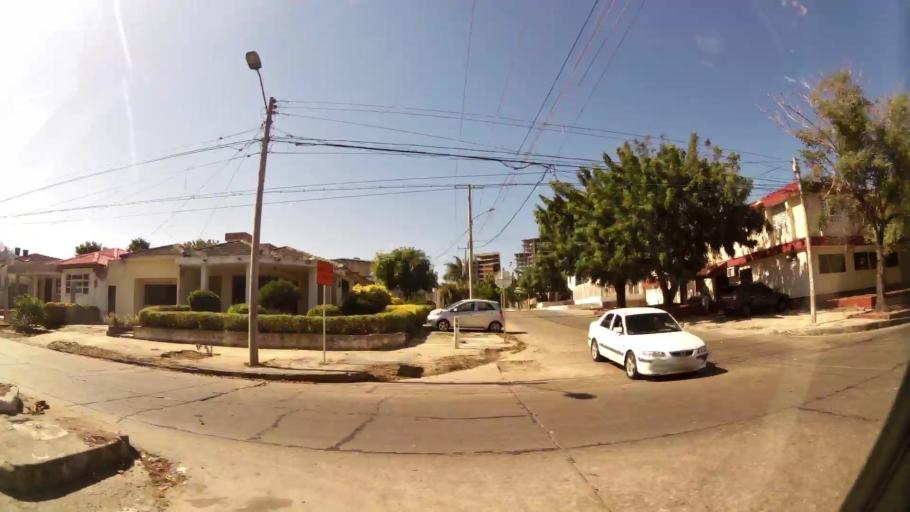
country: CO
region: Atlantico
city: Barranquilla
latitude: 10.9998
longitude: -74.7890
